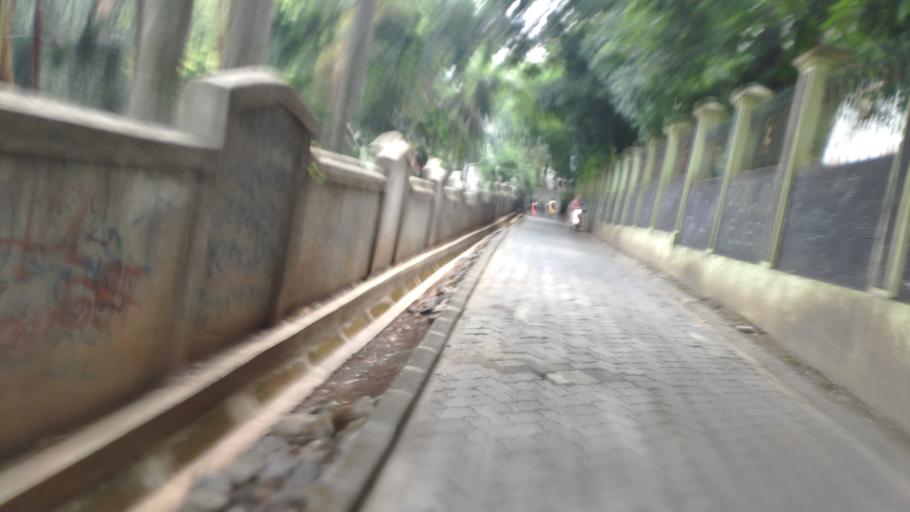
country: ID
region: Jakarta Raya
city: Jakarta
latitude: -6.3032
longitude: 106.8260
